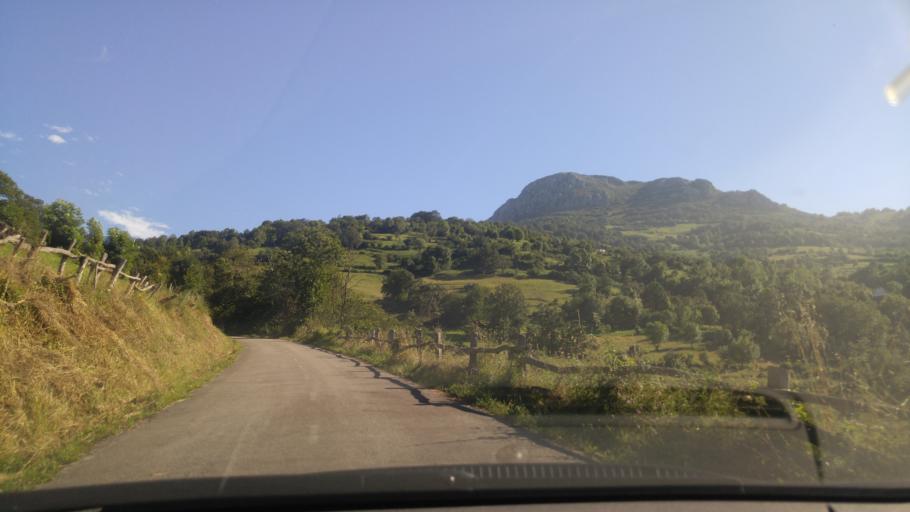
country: ES
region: Asturias
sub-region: Province of Asturias
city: Barzana
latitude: 43.1710
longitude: -5.9780
